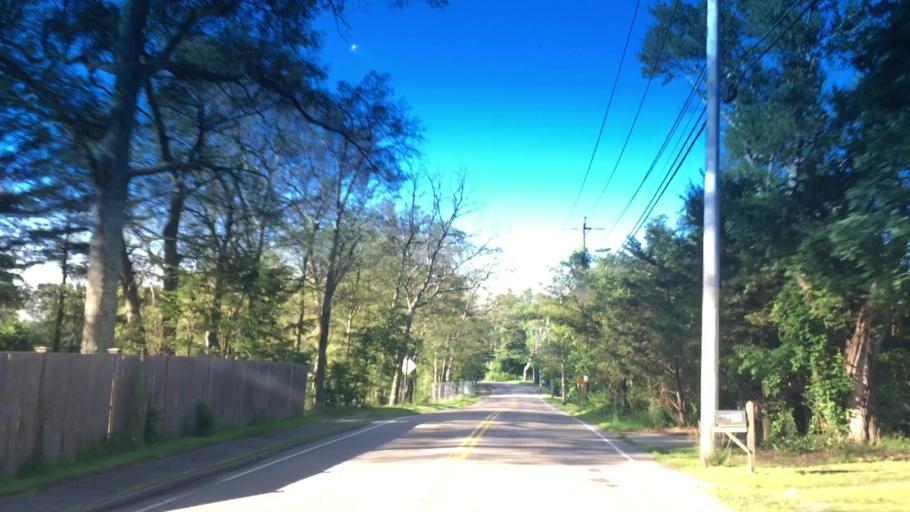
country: US
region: Massachusetts
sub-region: Norfolk County
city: Medway
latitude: 42.1526
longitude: -71.3918
